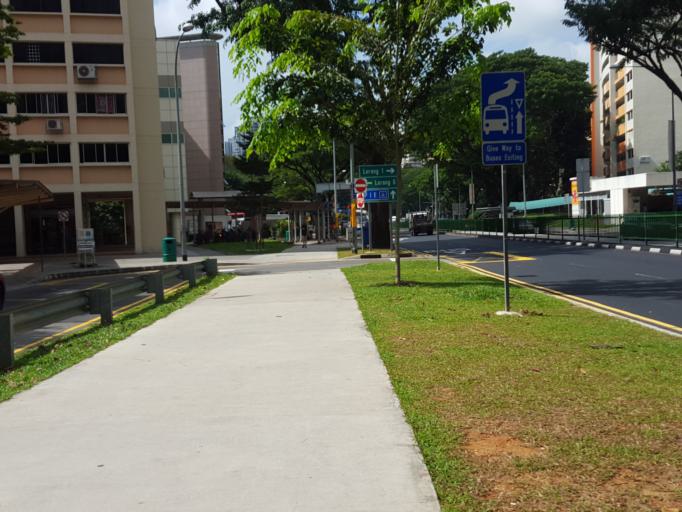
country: SG
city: Singapore
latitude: 1.3340
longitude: 103.8470
